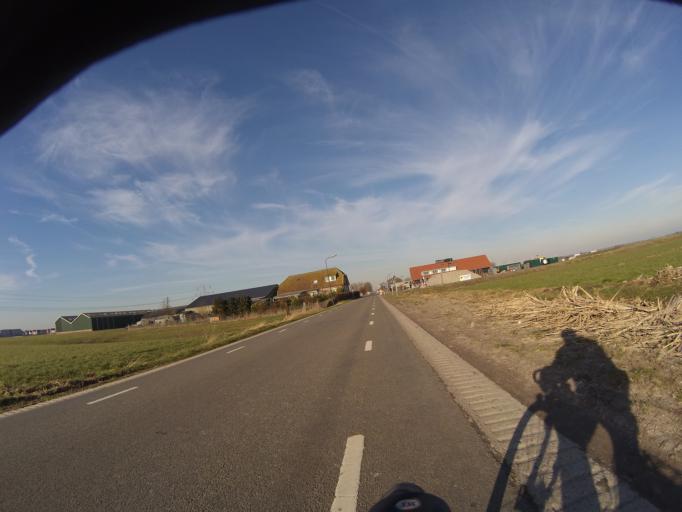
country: NL
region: Utrecht
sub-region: Gemeente Bunschoten
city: Bunschoten
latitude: 52.2283
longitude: 5.3911
